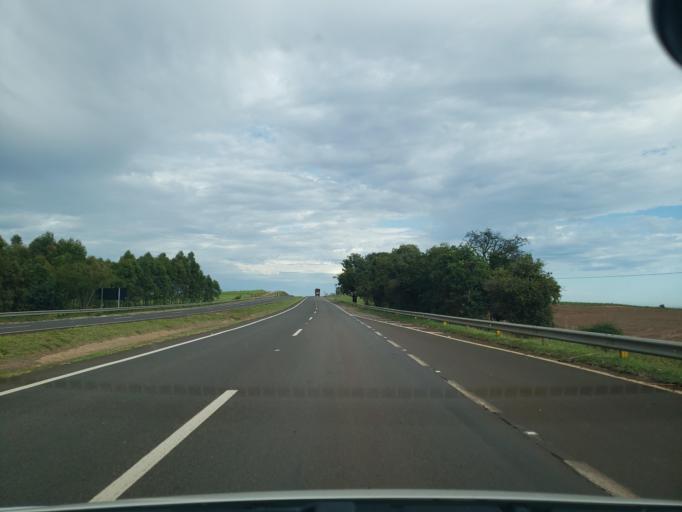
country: BR
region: Sao Paulo
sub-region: Jau
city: Jau
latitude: -22.2659
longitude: -48.4455
